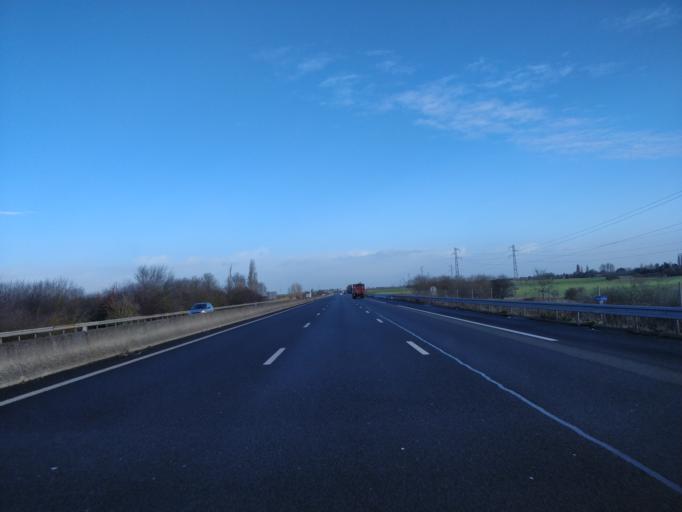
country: FR
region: Centre
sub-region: Departement du Loiret
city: Beaugency
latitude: 47.7964
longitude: 1.6097
